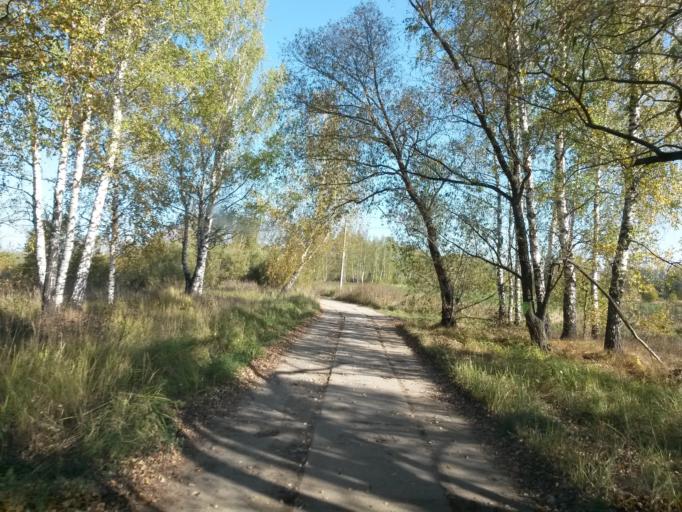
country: RU
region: Moskovskaya
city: Lyubuchany
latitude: 55.2578
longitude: 37.6224
